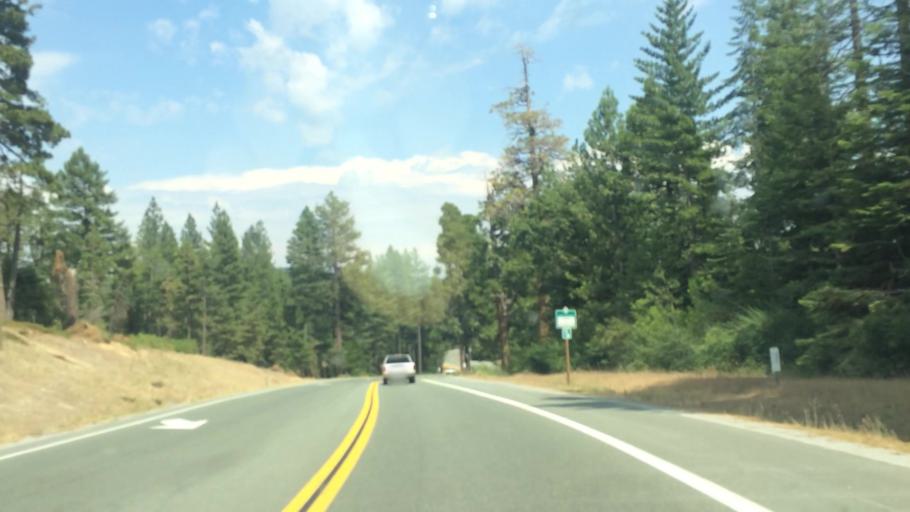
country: US
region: California
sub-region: Amador County
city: Pioneer
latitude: 38.5304
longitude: -120.4222
